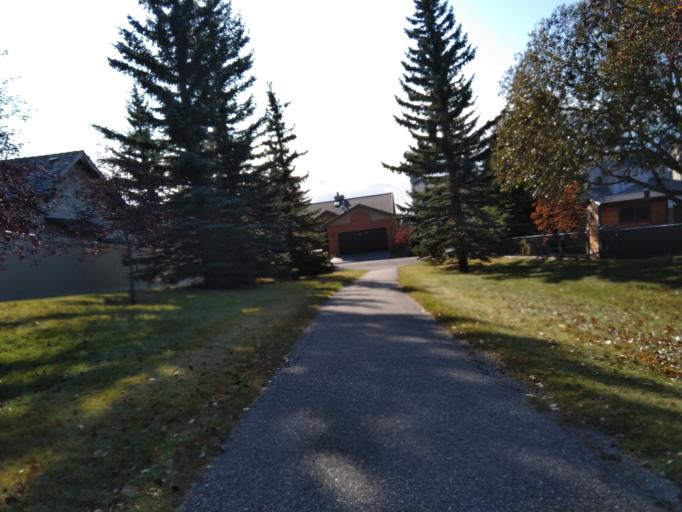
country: CA
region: Alberta
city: Calgary
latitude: 51.1297
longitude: -114.1513
